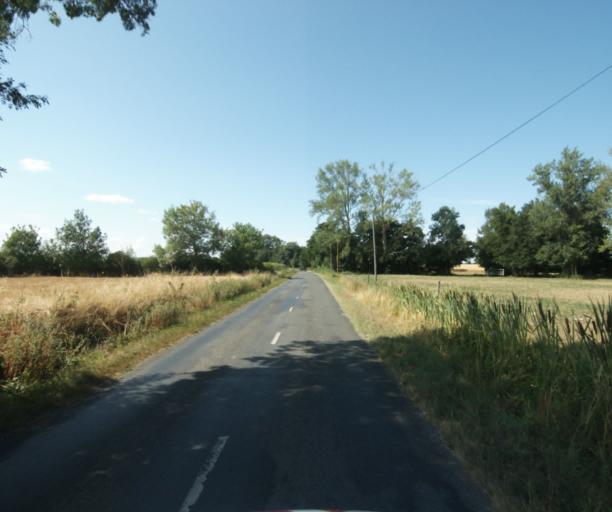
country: FR
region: Midi-Pyrenees
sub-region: Departement de la Haute-Garonne
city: Revel
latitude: 43.4809
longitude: 1.9890
